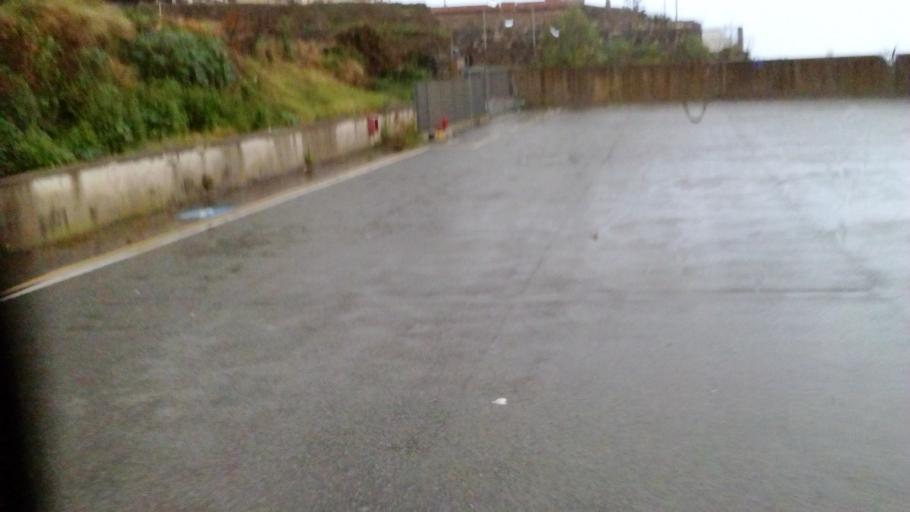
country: IT
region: Sicily
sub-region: Messina
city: Larderia
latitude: 38.1333
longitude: 15.5242
